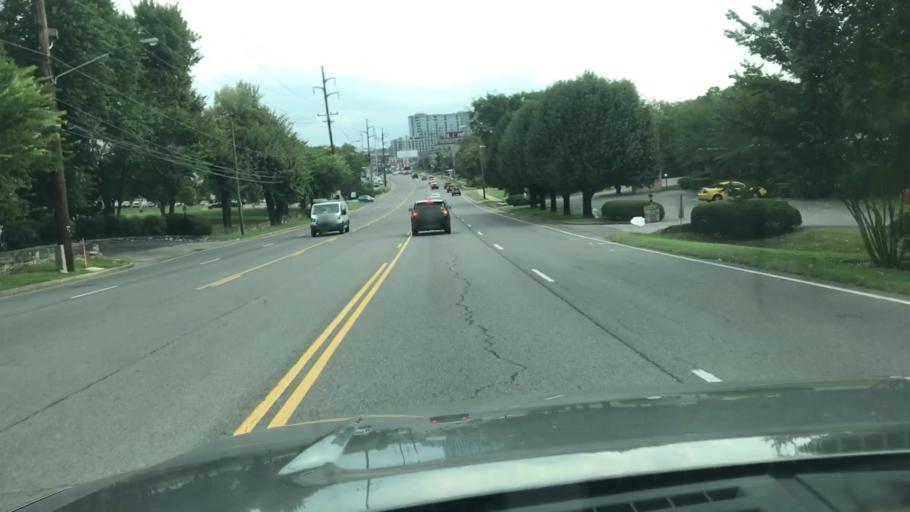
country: US
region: Tennessee
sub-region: Davidson County
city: Belle Meade
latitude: 36.0978
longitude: -86.8229
